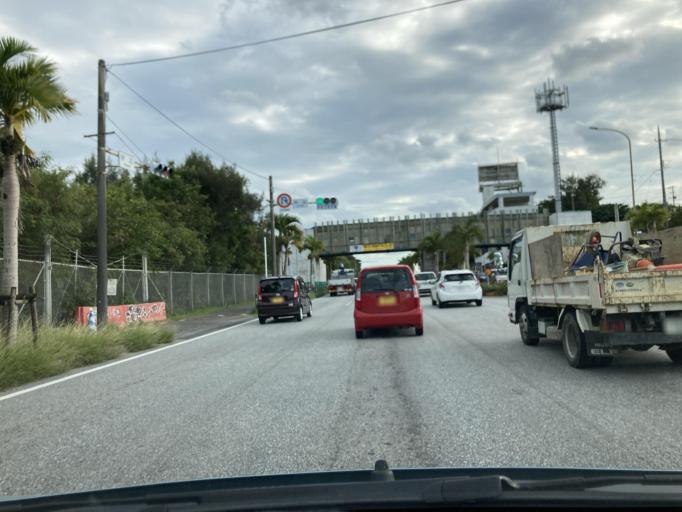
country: JP
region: Okinawa
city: Chatan
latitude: 26.3368
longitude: 127.7515
